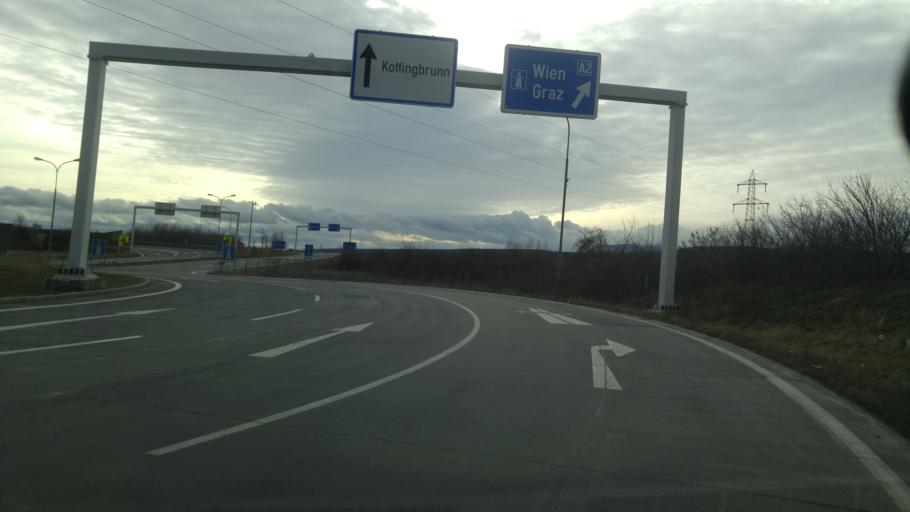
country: AT
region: Lower Austria
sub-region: Politischer Bezirk Baden
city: Kottingbrunn
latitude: 47.9552
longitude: 16.2187
